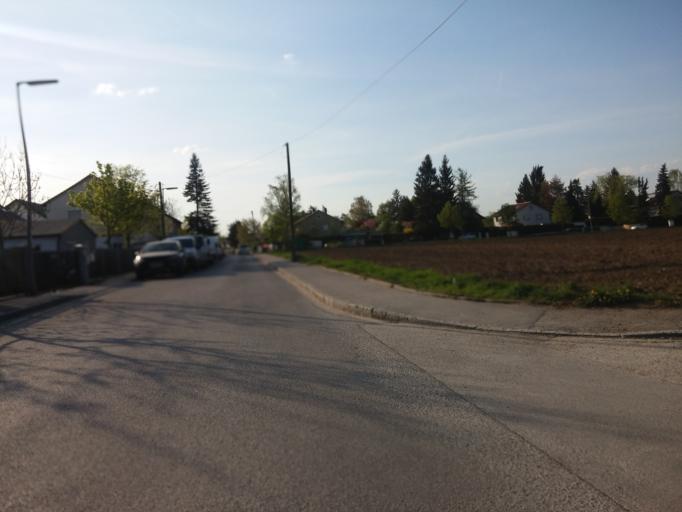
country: DE
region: Bavaria
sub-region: Upper Bavaria
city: Haar
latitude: 48.1285
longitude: 11.6778
